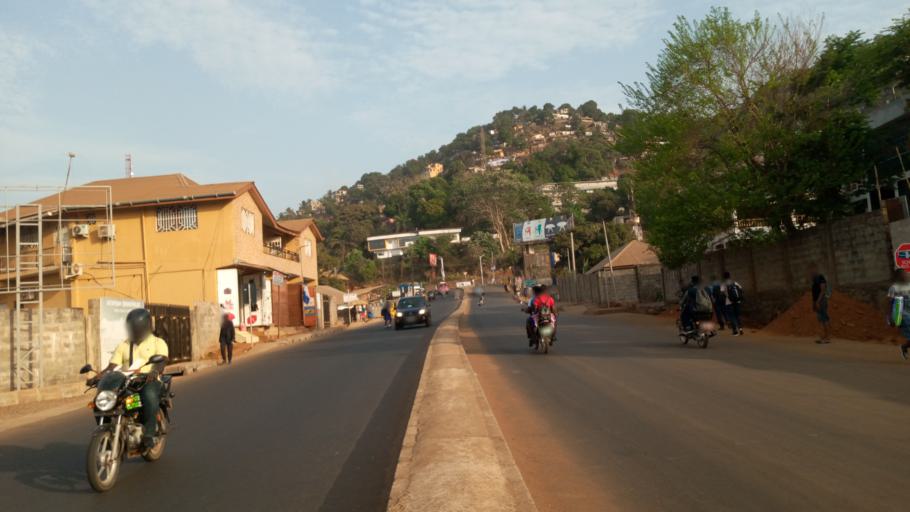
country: SL
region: Western Area
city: Freetown
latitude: 8.4704
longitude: -13.2463
